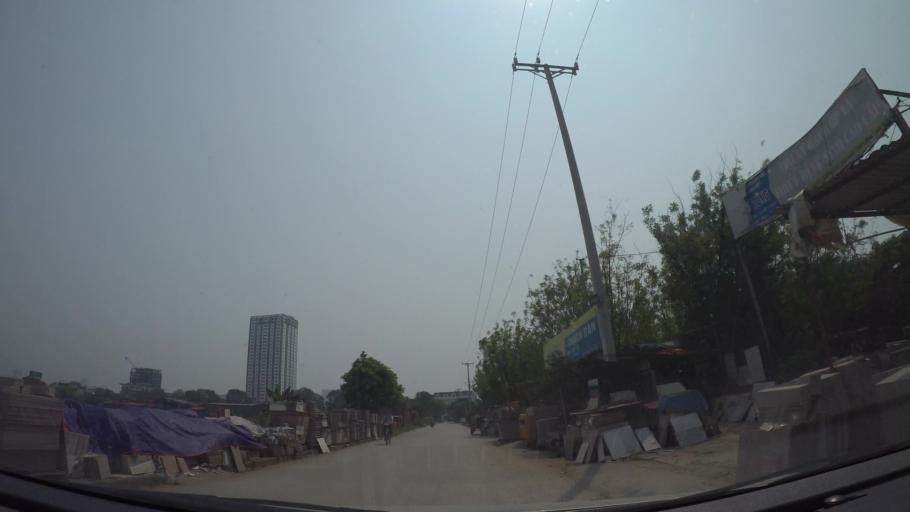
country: VN
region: Ha Noi
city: Ha Dong
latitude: 20.9897
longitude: 105.7680
